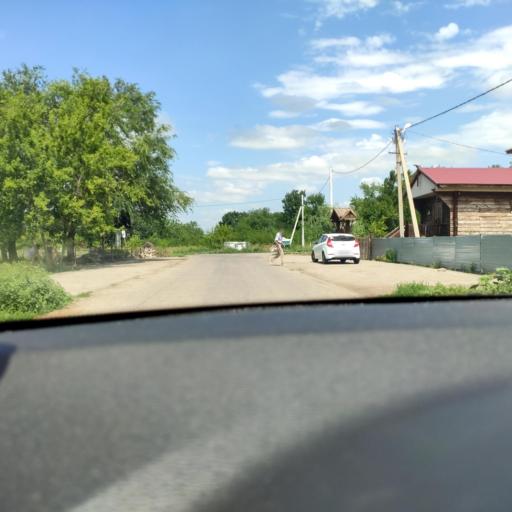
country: RU
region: Samara
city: Kinel'
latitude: 53.3383
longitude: 50.5295
